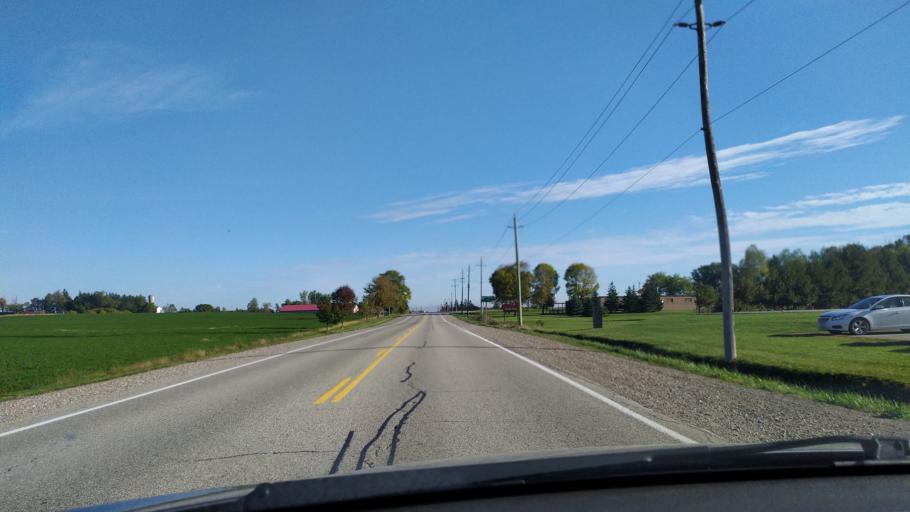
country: CA
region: Ontario
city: Stratford
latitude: 43.4770
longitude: -80.7812
